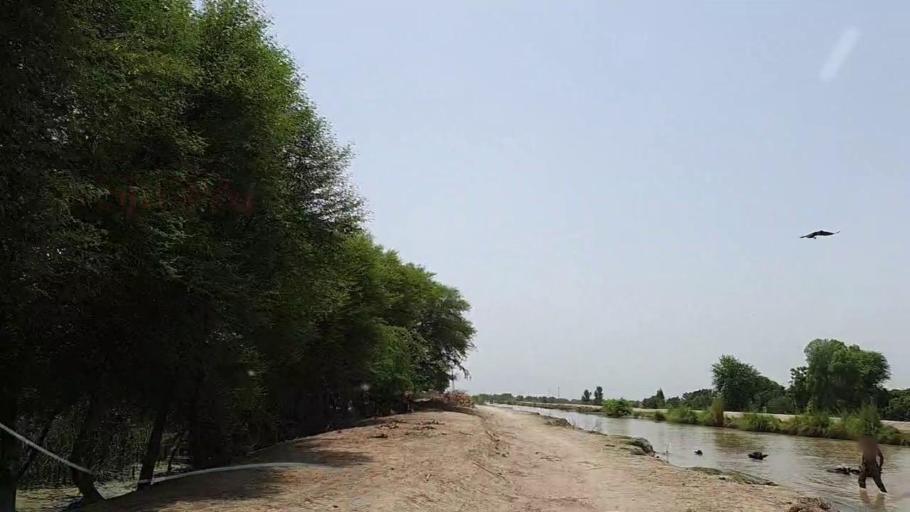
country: PK
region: Sindh
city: Tharu Shah
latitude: 26.9916
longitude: 68.0991
